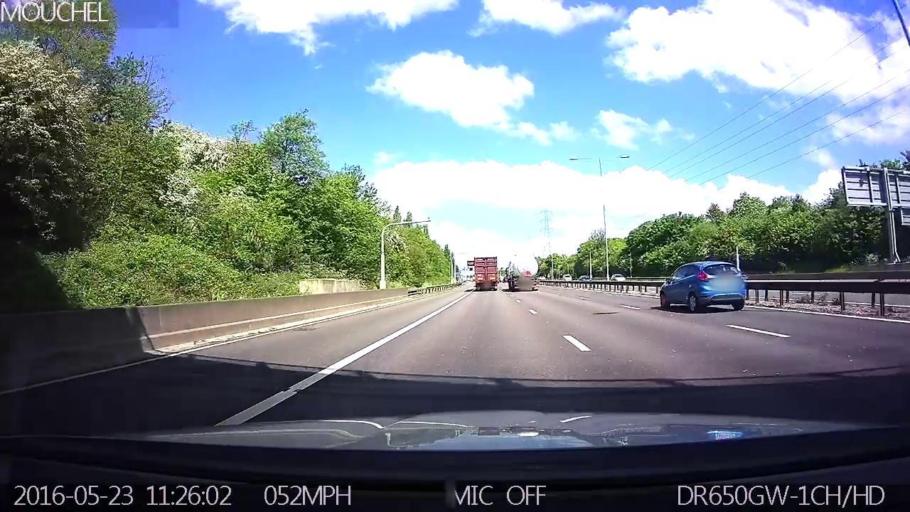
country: GB
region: England
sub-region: Walsall
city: Bloxwich
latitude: 52.5995
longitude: -2.0162
